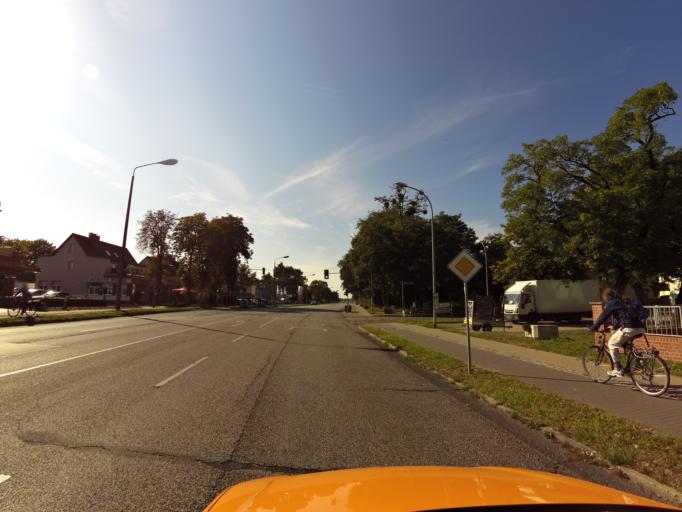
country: DE
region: Brandenburg
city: Stahnsdorf
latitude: 52.3855
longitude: 13.1961
